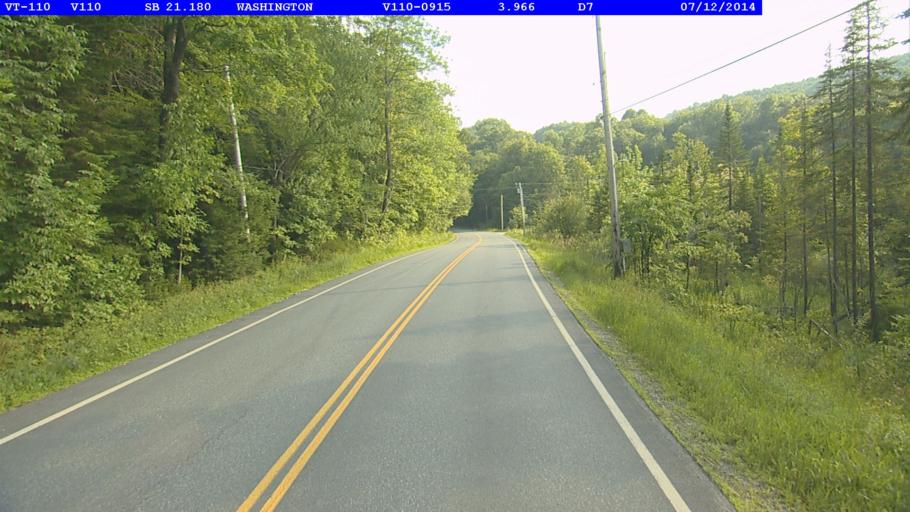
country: US
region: Vermont
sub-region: Orange County
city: Williamstown
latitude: 44.0914
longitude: -72.4580
